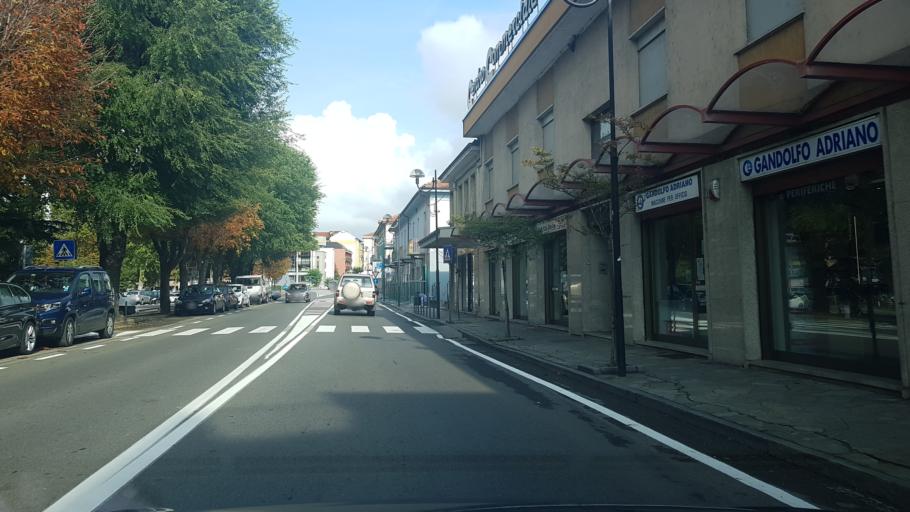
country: IT
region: Piedmont
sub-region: Provincia di Asti
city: Canelli
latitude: 44.7173
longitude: 8.2857
